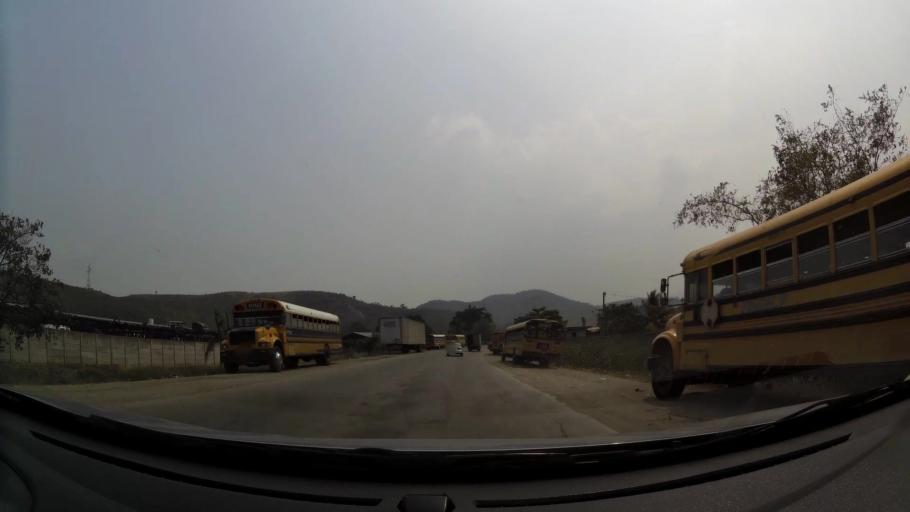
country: HN
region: Cortes
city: Chotepe
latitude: 15.4637
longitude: -87.9636
